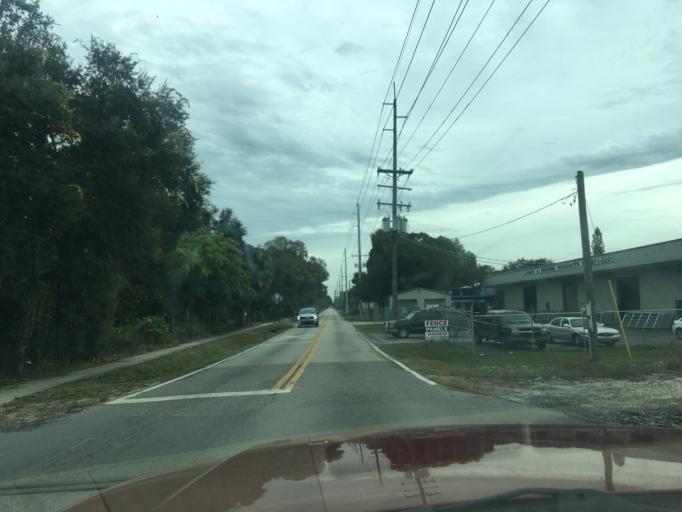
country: US
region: Florida
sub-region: Hillsborough County
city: Gibsonton
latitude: 27.8461
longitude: -82.3808
